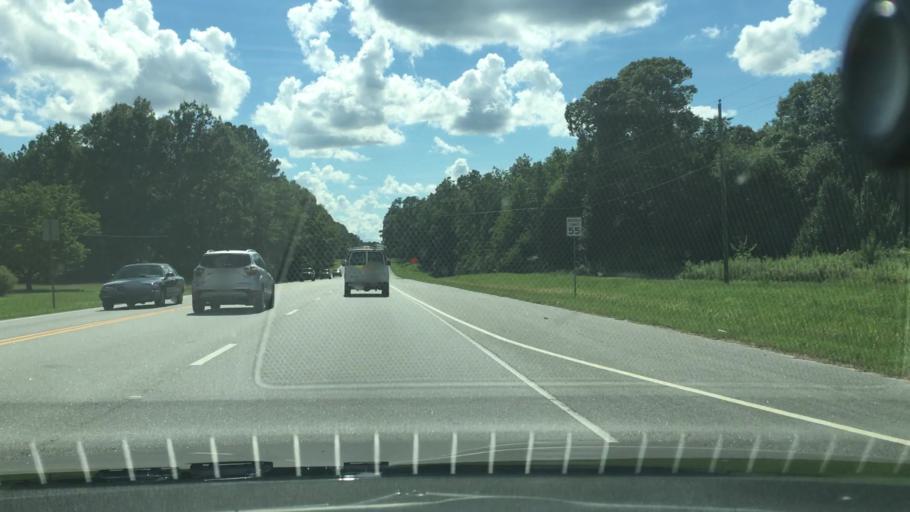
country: US
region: Georgia
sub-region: Butts County
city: Jackson
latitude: 33.2918
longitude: -83.9886
